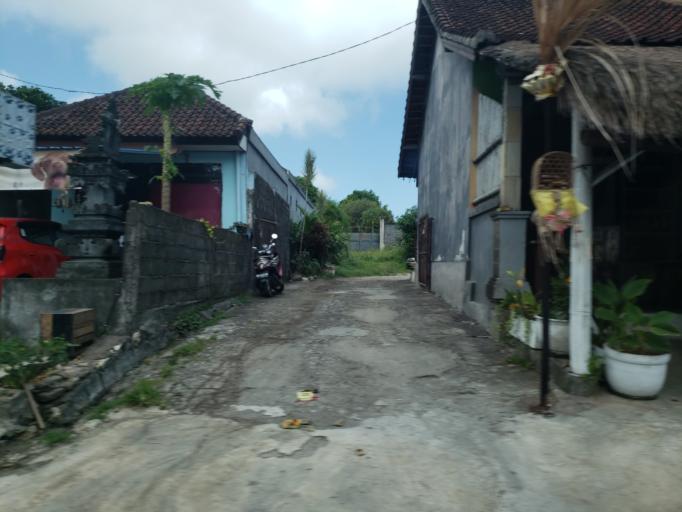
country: ID
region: Bali
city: Kangin
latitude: -8.8272
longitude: 115.1395
